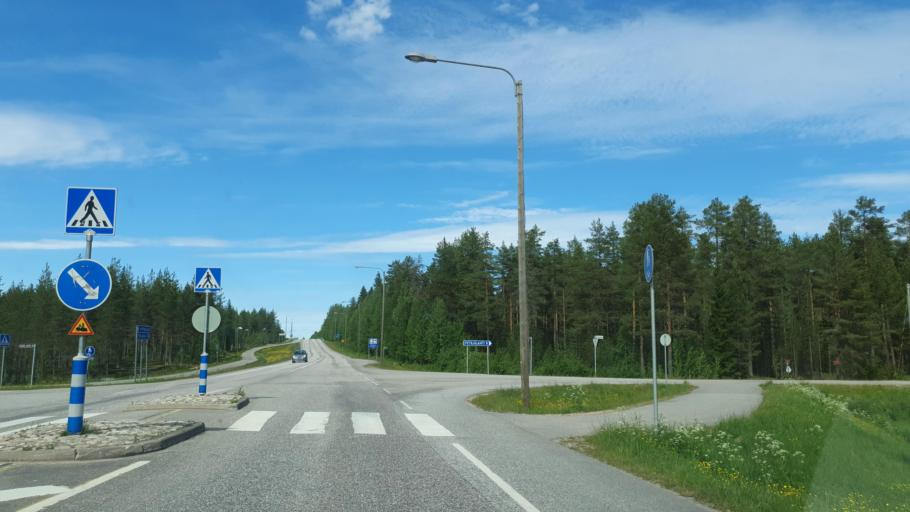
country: FI
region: Kainuu
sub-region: Kehys-Kainuu
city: Hyrynsalmi
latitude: 64.6912
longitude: 28.4759
